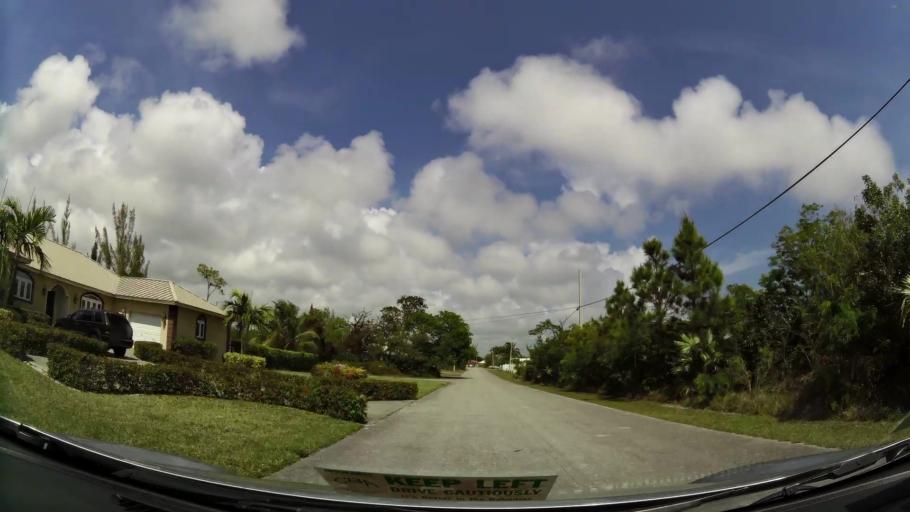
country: BS
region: Freeport
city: Freeport
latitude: 26.5065
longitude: -78.7126
